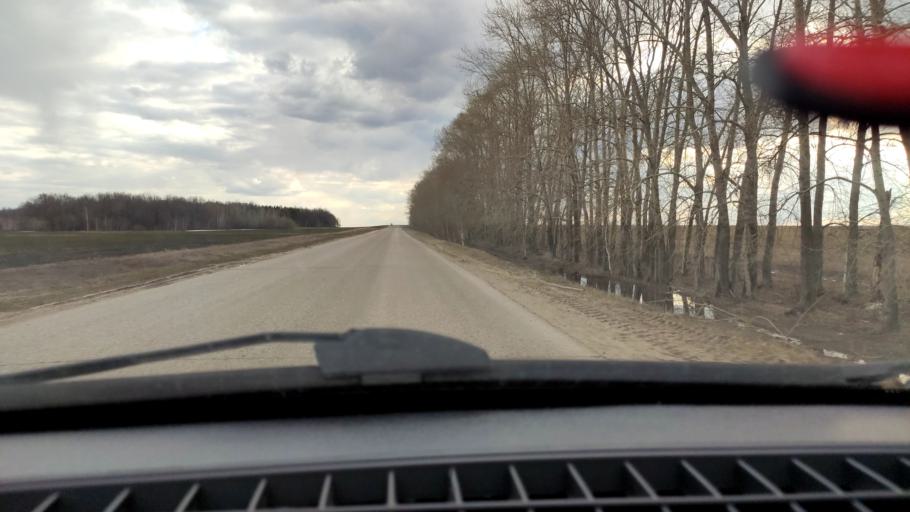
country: RU
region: Bashkortostan
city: Karmaskaly
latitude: 54.3044
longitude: 55.9333
